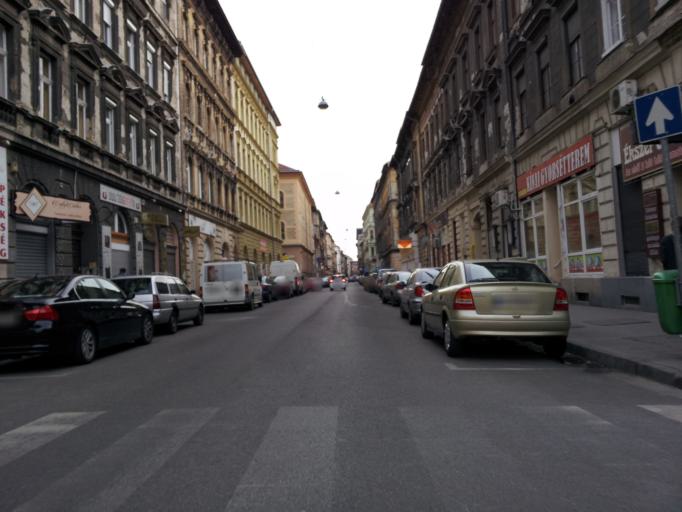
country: HU
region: Budapest
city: Budapest VI. keruelet
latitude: 47.5121
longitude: 19.0671
